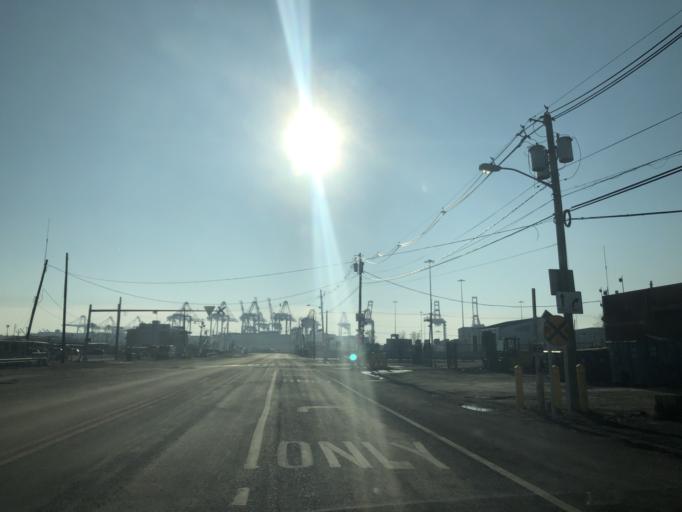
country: US
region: New Jersey
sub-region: Hudson County
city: Bayonne
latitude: 40.6910
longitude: -74.1430
